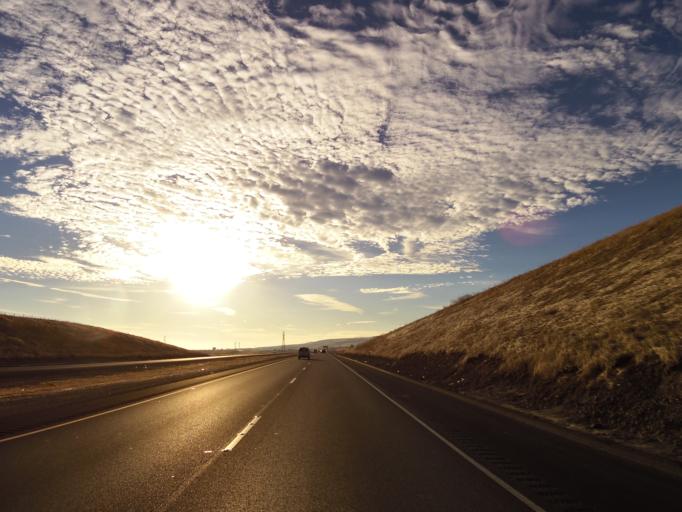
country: US
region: California
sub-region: San Joaquin County
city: Mountain House
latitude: 37.7312
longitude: -121.5485
